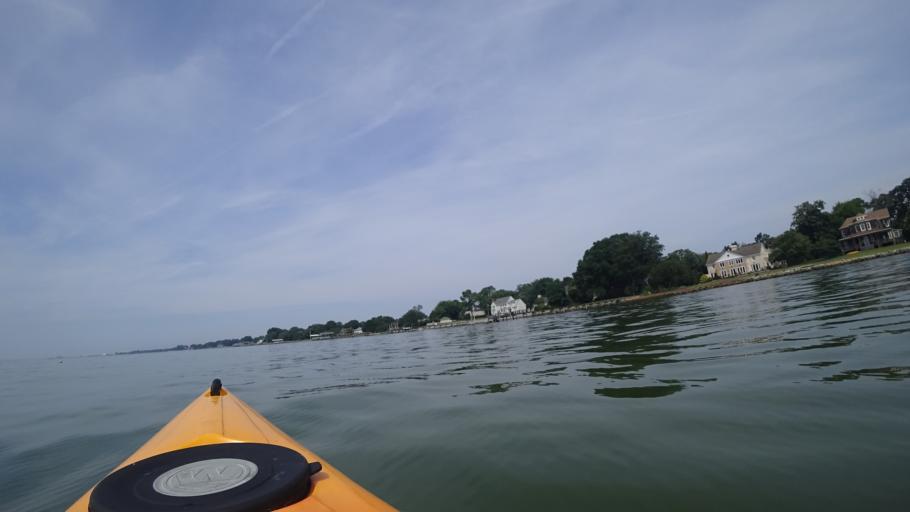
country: US
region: Virginia
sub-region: City of Hampton
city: Hampton
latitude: 36.9985
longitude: -76.3737
